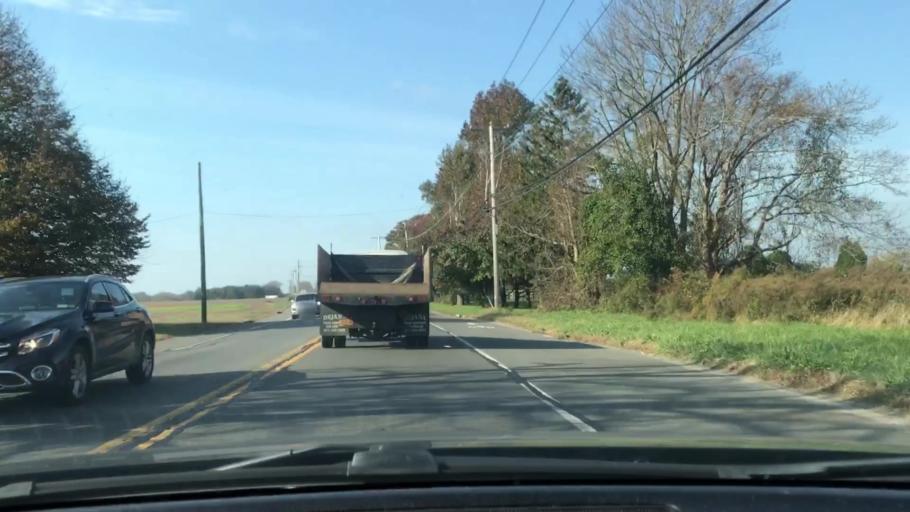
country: US
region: New York
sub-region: Suffolk County
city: Bridgehampton
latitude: 40.9442
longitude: -72.2670
